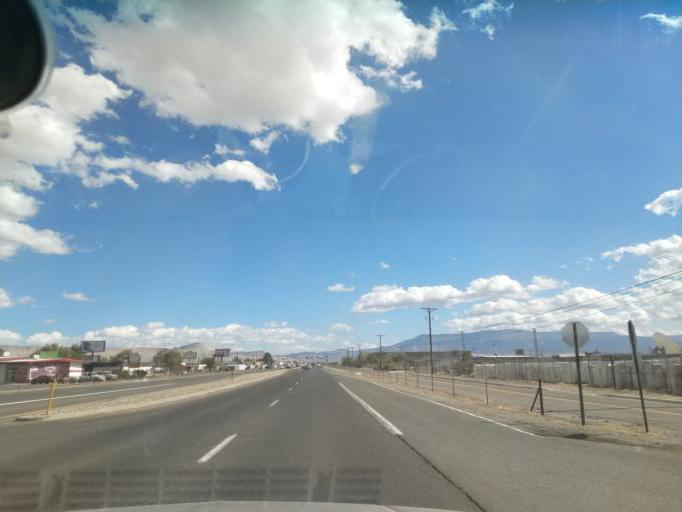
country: US
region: Colorado
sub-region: Mesa County
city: Grand Junction
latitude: 39.0681
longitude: -108.5375
